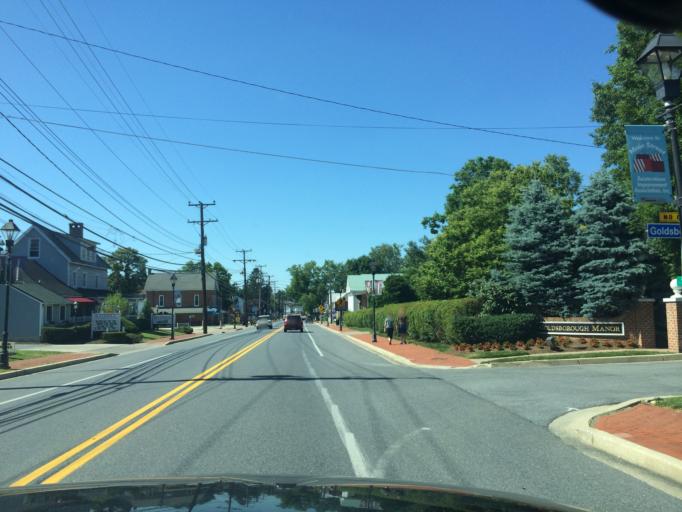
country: US
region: Maryland
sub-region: Baltimore County
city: Reisterstown
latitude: 39.4604
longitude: -76.8275
